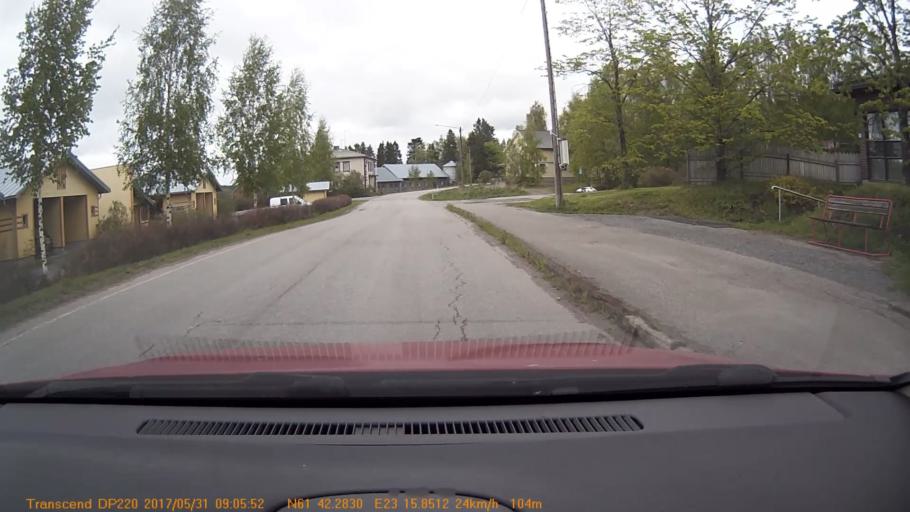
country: FI
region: Pirkanmaa
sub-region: Tampere
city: Viljakkala
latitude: 61.7047
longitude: 23.2641
